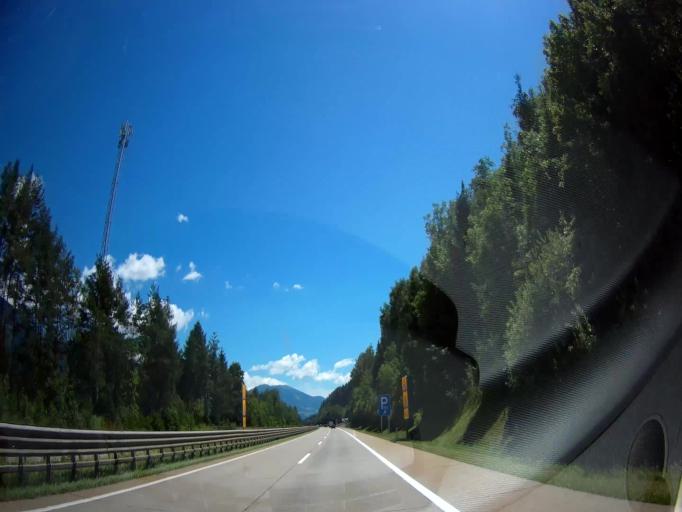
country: AT
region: Carinthia
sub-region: Politischer Bezirk Spittal an der Drau
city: Seeboden
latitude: 46.8126
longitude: 13.5033
